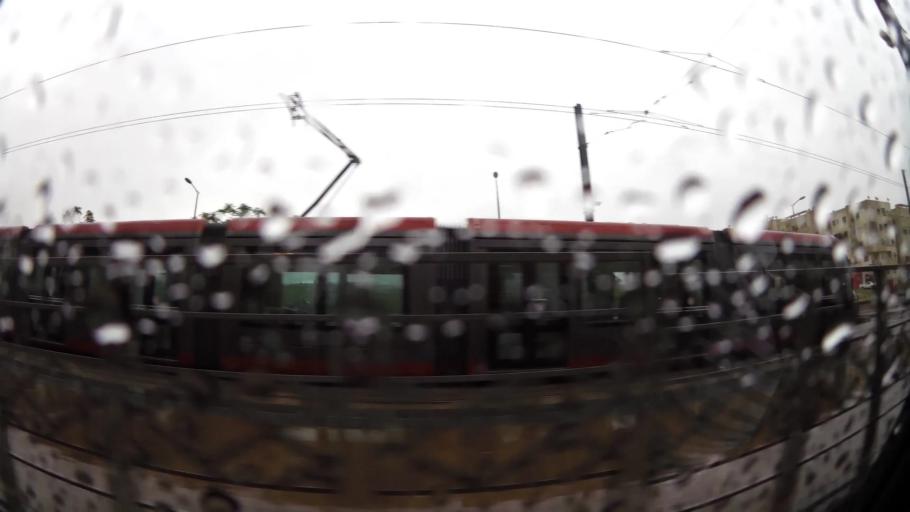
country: MA
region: Grand Casablanca
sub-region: Mediouna
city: Tit Mellil
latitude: 33.5870
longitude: -7.5015
